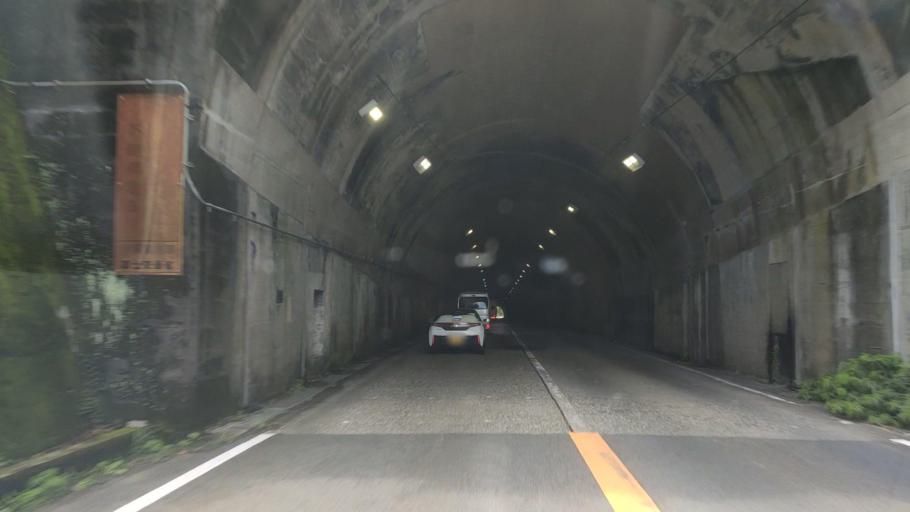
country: JP
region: Mie
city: Owase
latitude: 34.1704
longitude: 136.2905
